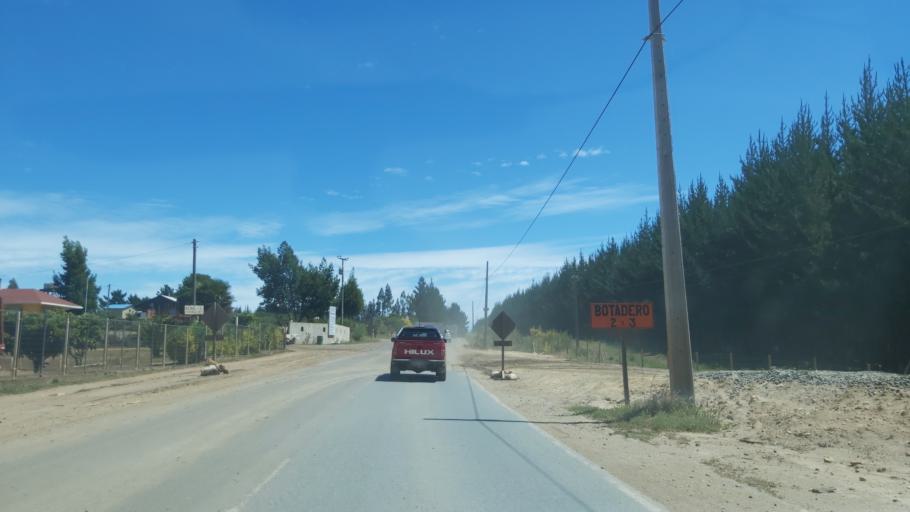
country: CL
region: Maule
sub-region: Provincia de Talca
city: Constitucion
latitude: -35.3918
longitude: -72.4253
